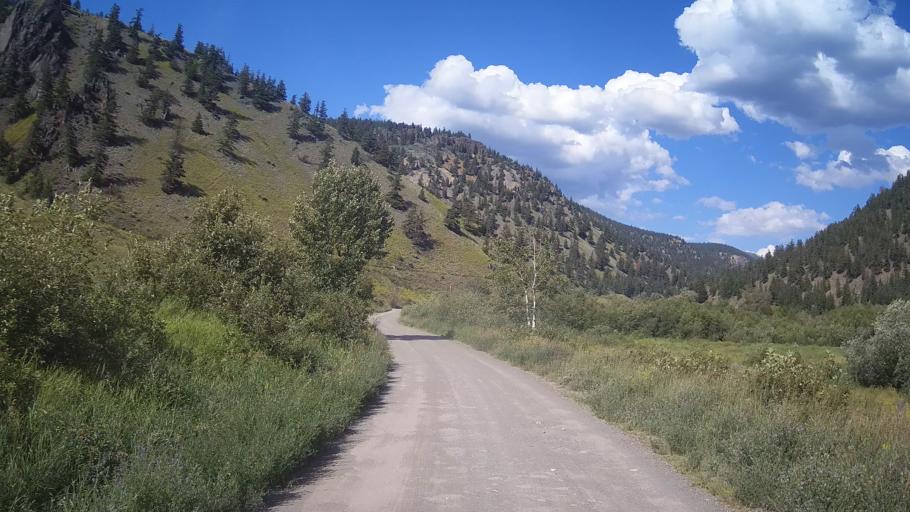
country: CA
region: British Columbia
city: Lillooet
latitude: 51.2403
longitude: -122.0433
